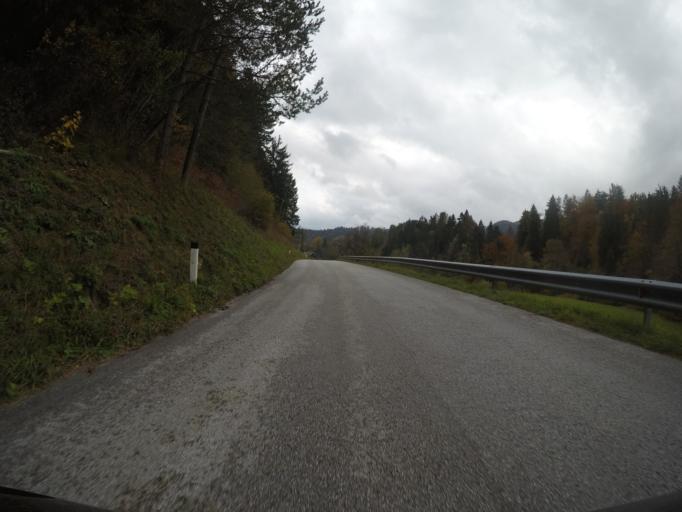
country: SI
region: Gorje
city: Zgornje Gorje
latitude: 46.3796
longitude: 14.0509
